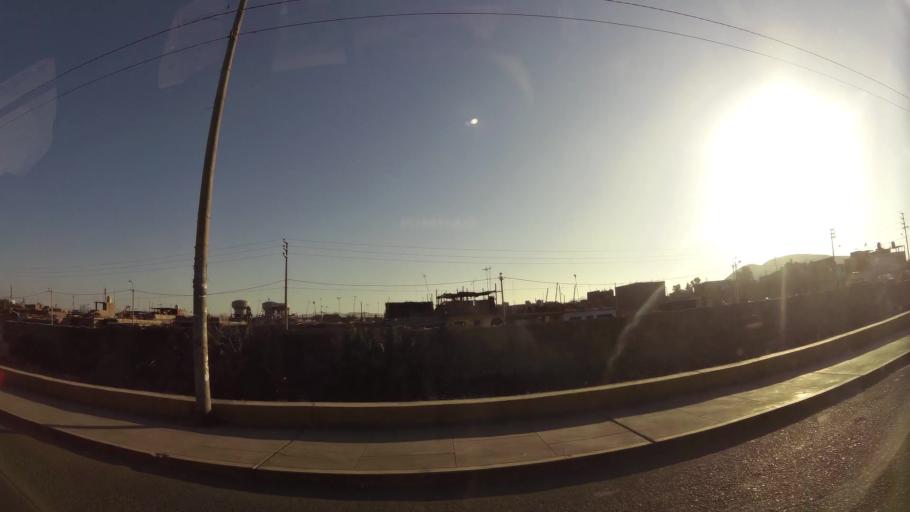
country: PE
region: Ica
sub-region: Provincia de Ica
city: Ica
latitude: -14.0561
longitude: -75.7263
